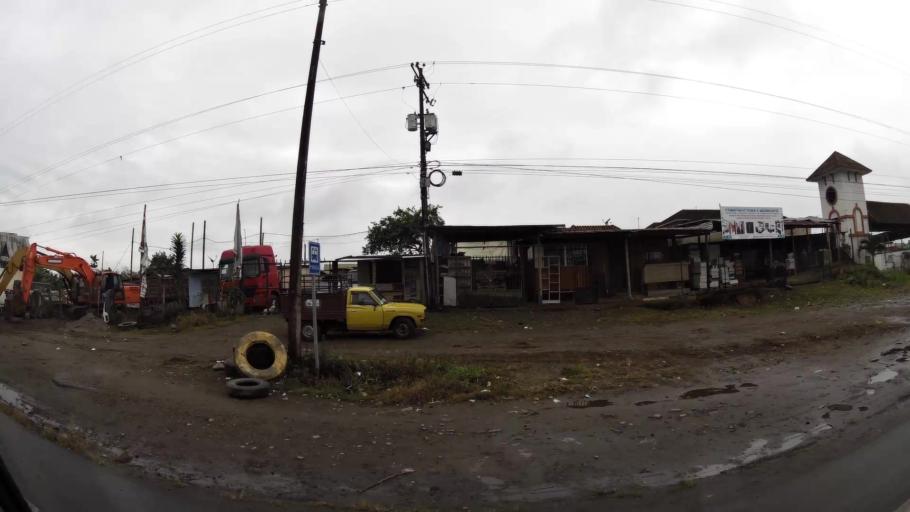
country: EC
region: Santo Domingo de los Tsachilas
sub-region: Canton Santo Domingo de los Colorados
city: Santo Domingo de los Colorados
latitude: -0.2416
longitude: -79.1905
